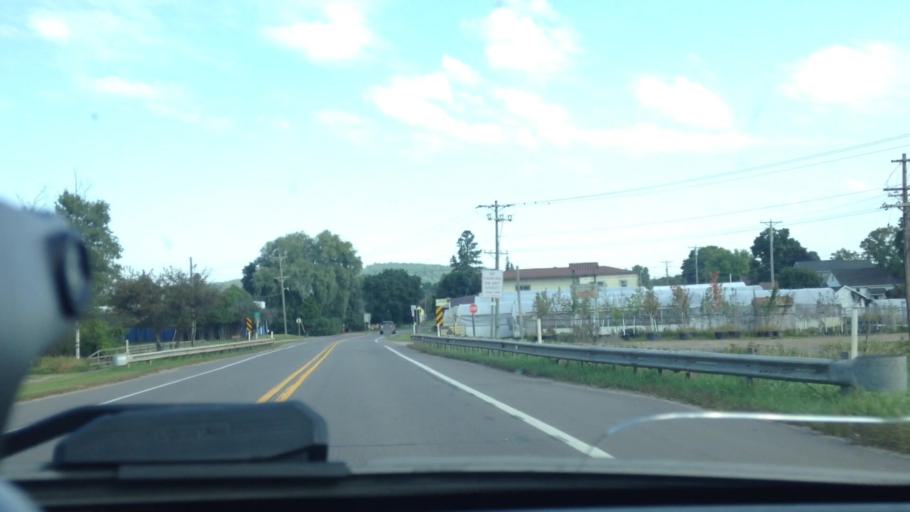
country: US
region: Michigan
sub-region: Dickinson County
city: Norway
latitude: 45.7798
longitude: -87.9095
